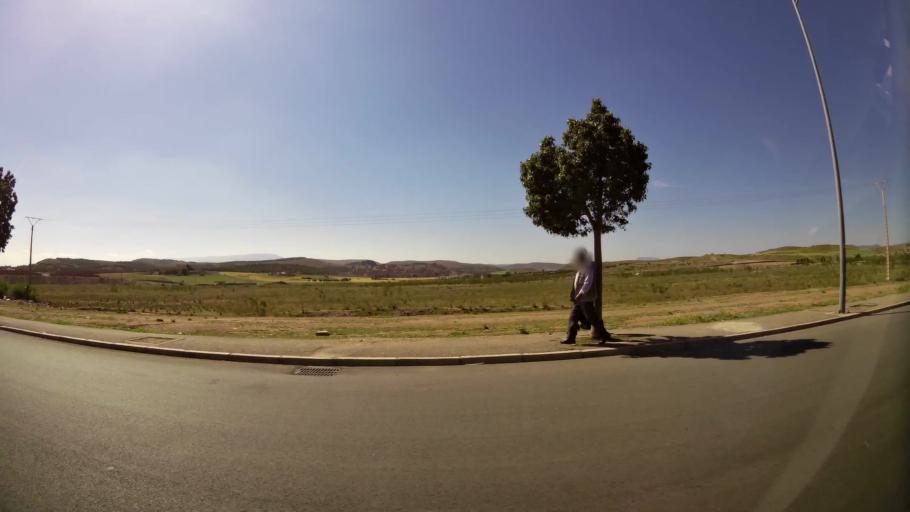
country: MA
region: Oriental
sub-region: Oujda-Angad
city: Oujda
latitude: 34.6517
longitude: -1.9377
